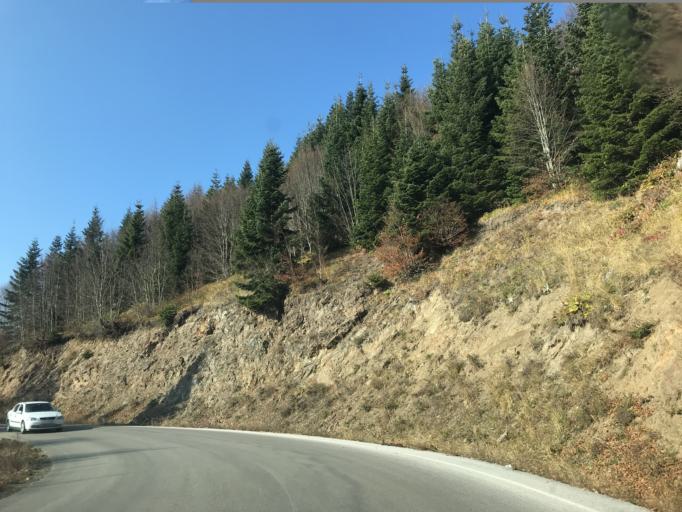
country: TR
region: Bolu
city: Bolu
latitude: 40.8866
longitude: 31.6818
